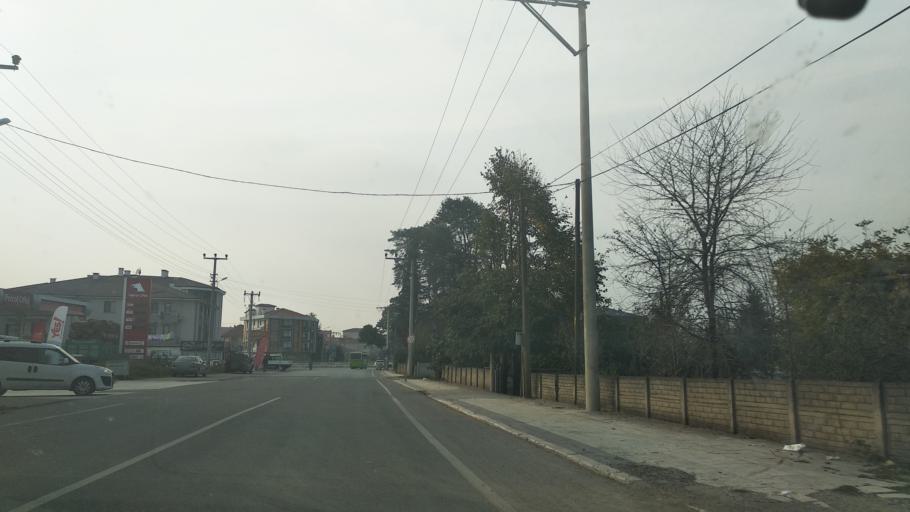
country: TR
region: Duzce
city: Duzce
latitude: 40.8310
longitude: 31.1699
